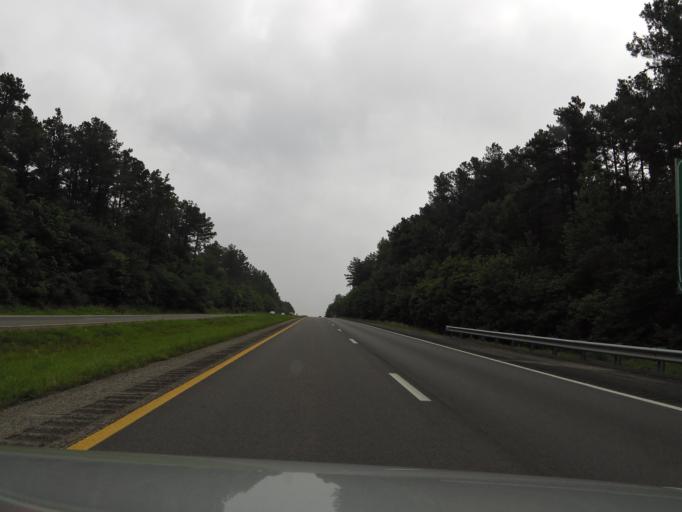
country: US
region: Kentucky
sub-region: Muhlenberg County
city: Morehead
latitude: 37.2498
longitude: -87.2230
